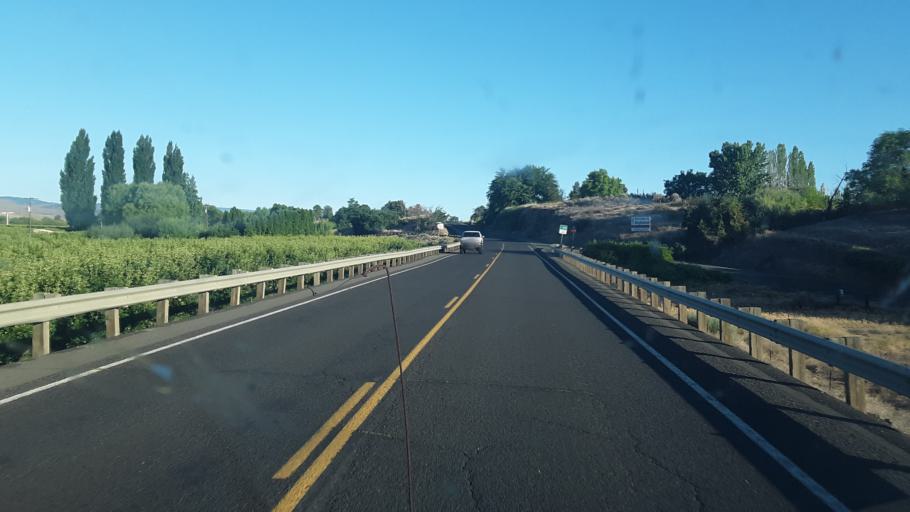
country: US
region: Washington
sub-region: Yakima County
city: Tieton
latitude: 46.6499
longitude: -120.7037
